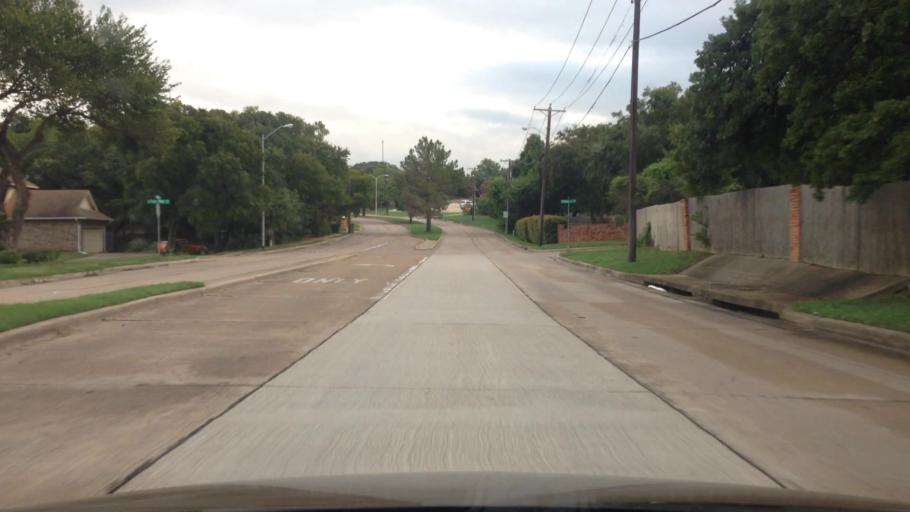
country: US
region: Texas
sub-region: Johnson County
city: Burleson
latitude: 32.5564
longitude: -97.3416
